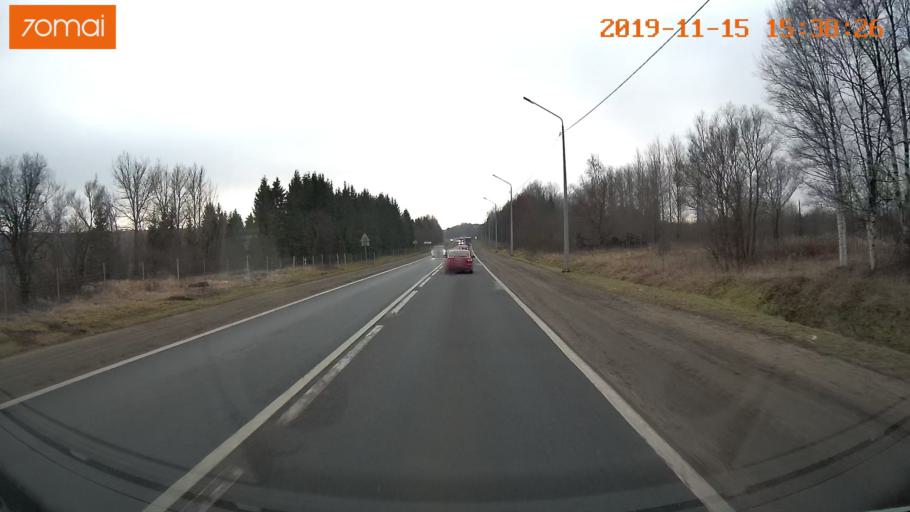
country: RU
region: Jaroslavl
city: Danilov
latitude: 58.0299
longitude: 40.0805
